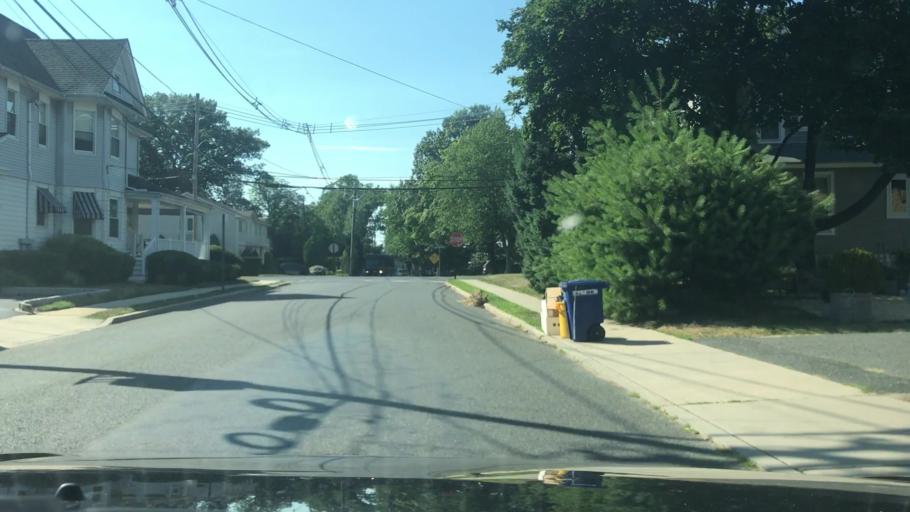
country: US
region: New Jersey
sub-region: Monmouth County
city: Red Bank
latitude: 40.3537
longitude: -74.0572
